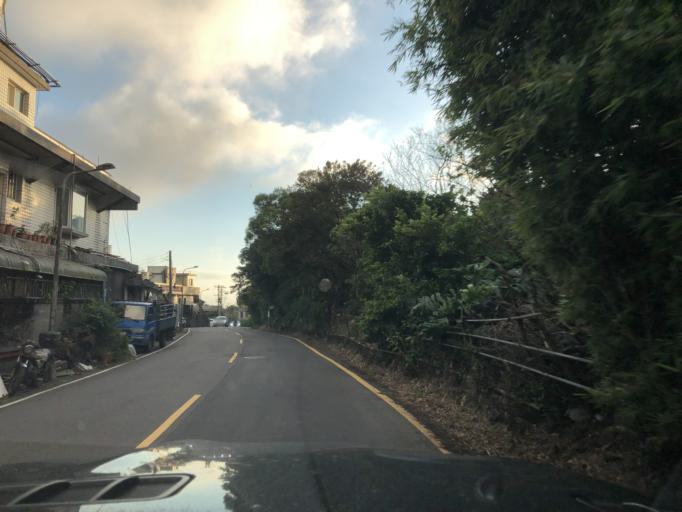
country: TW
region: Taipei
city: Taipei
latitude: 25.1487
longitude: 121.5594
